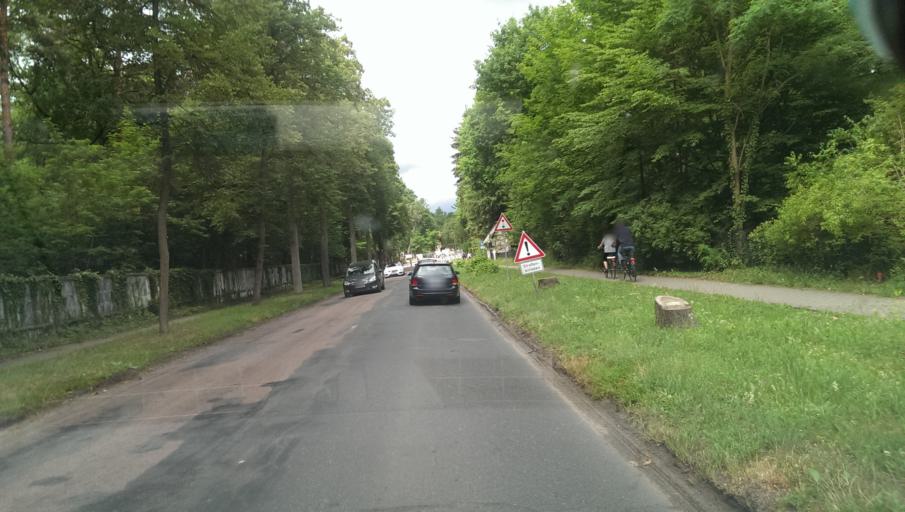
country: DE
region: Brandenburg
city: Fichtenwalde
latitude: 52.2637
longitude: 12.9231
